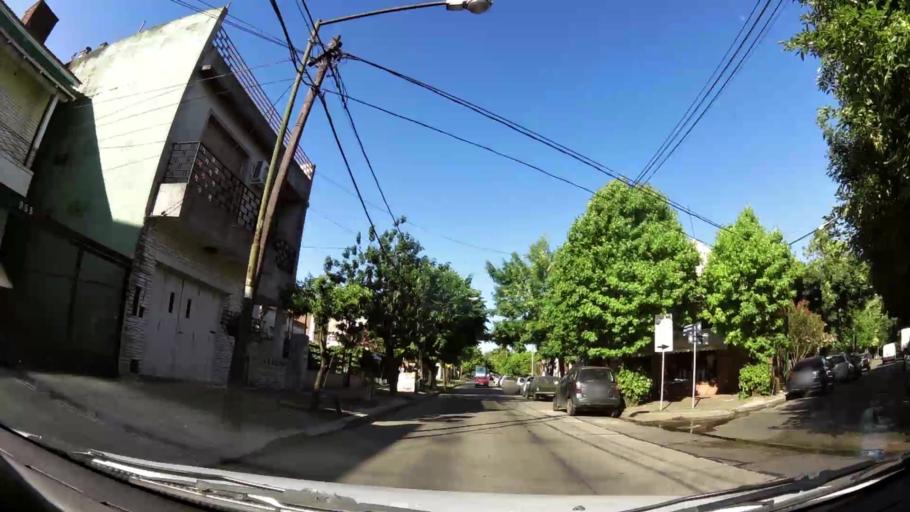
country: AR
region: Buenos Aires
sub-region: Partido de San Isidro
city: San Isidro
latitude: -34.4766
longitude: -58.5281
